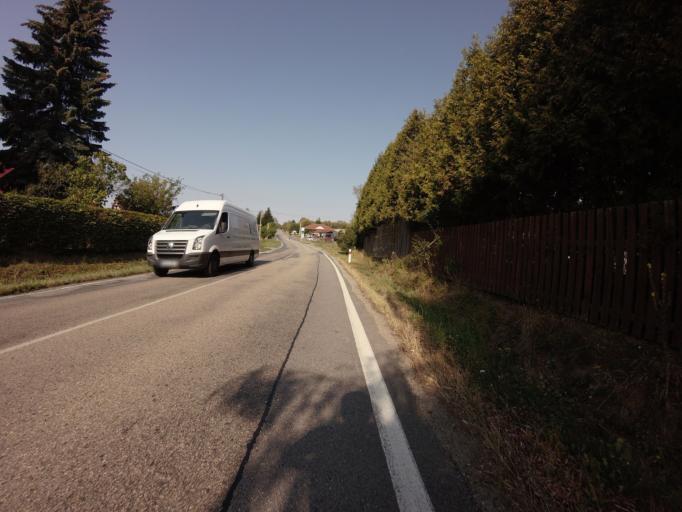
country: CZ
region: Central Bohemia
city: Tynec nad Sazavou
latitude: 49.8236
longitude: 14.6301
